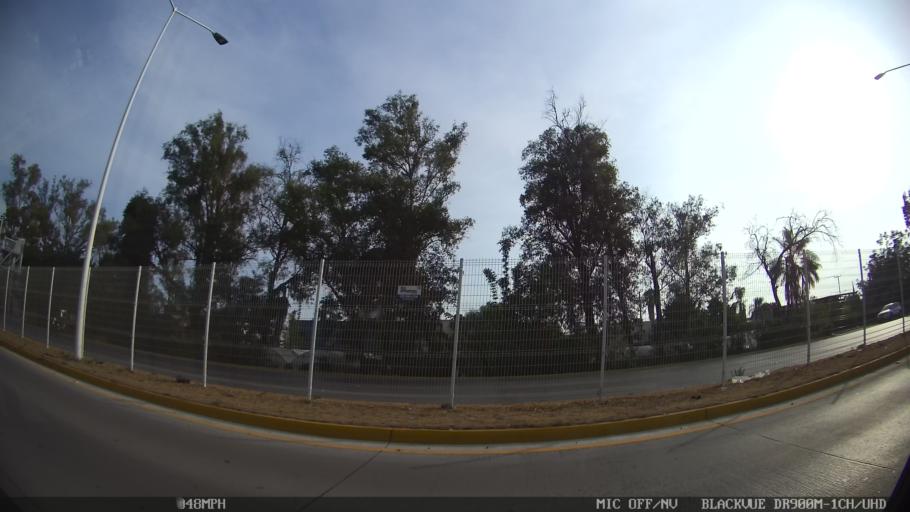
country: MX
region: Jalisco
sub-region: Zapopan
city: Zapopan
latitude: 20.7365
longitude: -103.3716
